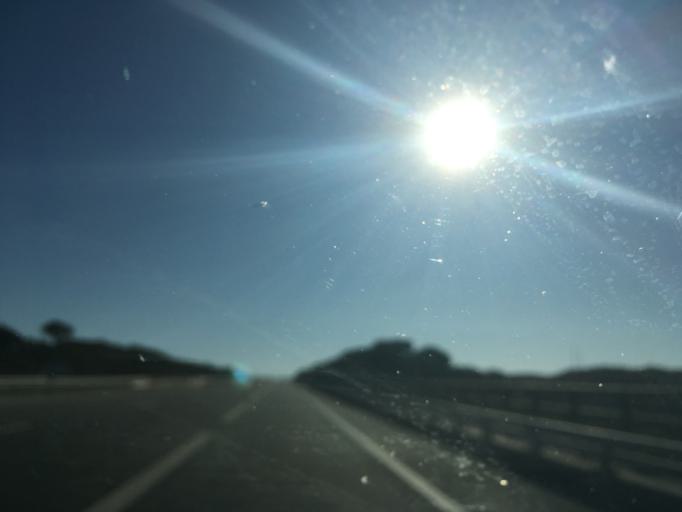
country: PT
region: Evora
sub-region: Estremoz
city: Estremoz
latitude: 38.7683
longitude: -7.6992
